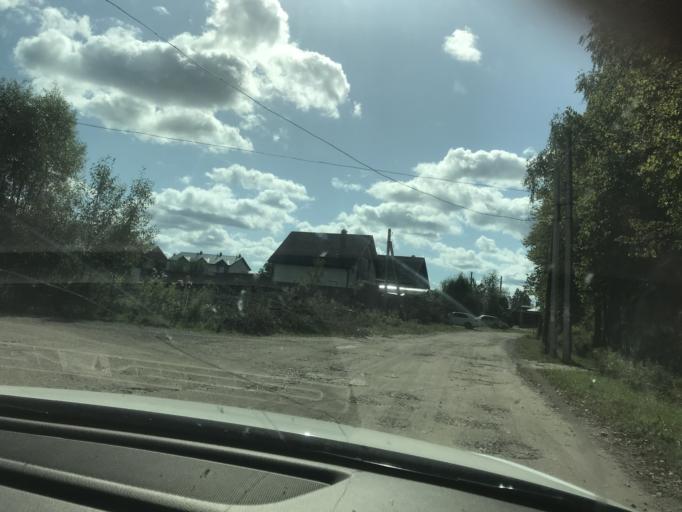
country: RU
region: Kaluga
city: Kondrovo
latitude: 54.7822
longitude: 35.9471
